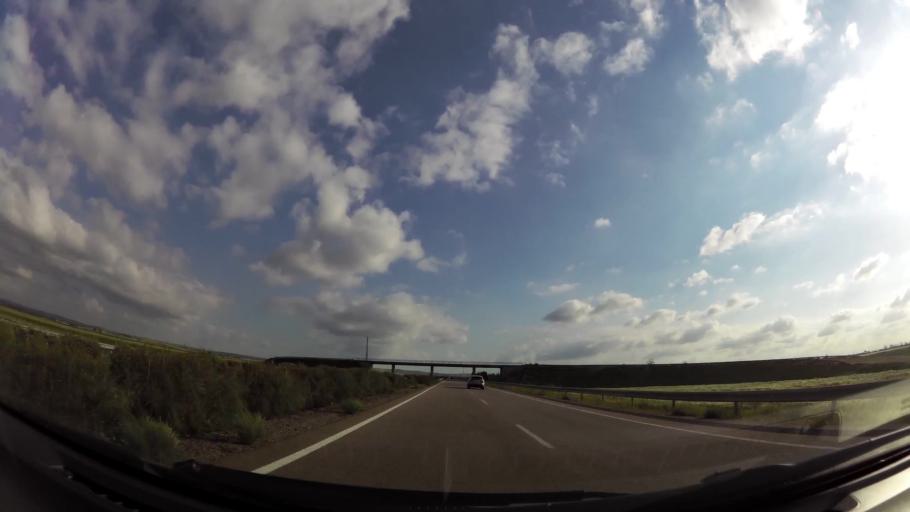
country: MA
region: Chaouia-Ouardigha
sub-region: Settat Province
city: Berrechid
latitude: 33.1480
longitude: -7.5731
